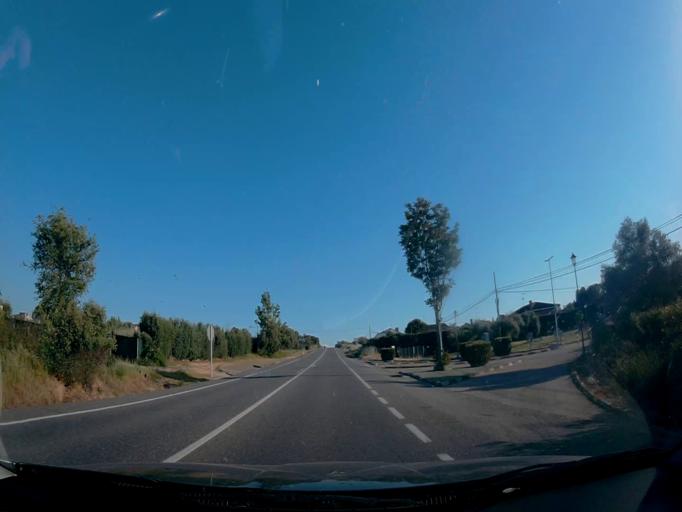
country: ES
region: Castille-La Mancha
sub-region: Province of Toledo
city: Escalona
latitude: 40.1422
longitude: -4.4036
